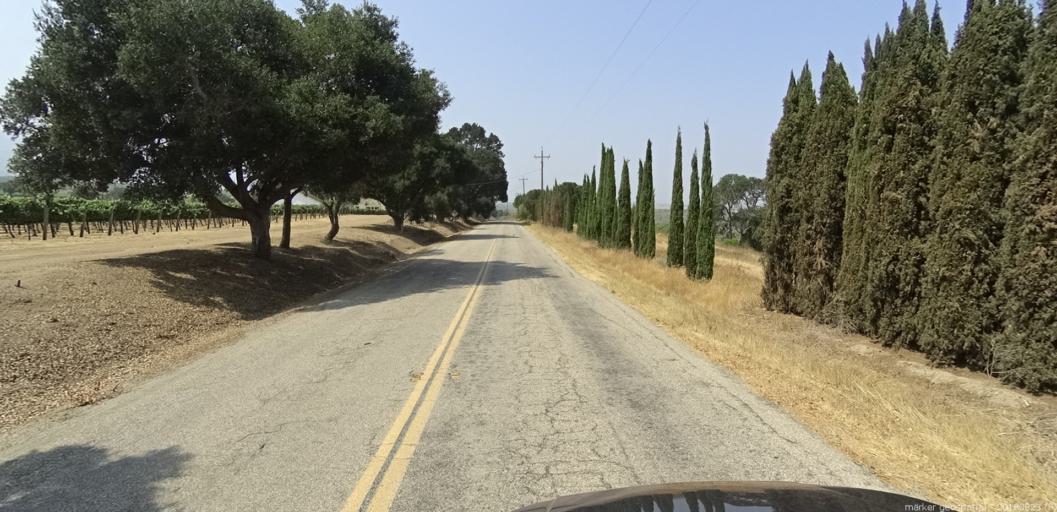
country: US
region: California
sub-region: Monterey County
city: Gonzales
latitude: 36.4451
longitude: -121.4316
